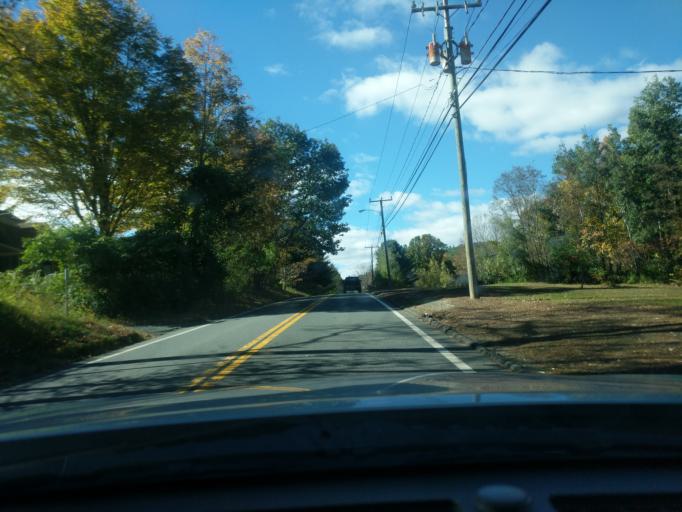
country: US
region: Massachusetts
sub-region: Hampden County
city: Granville
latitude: 42.1689
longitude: -72.8770
